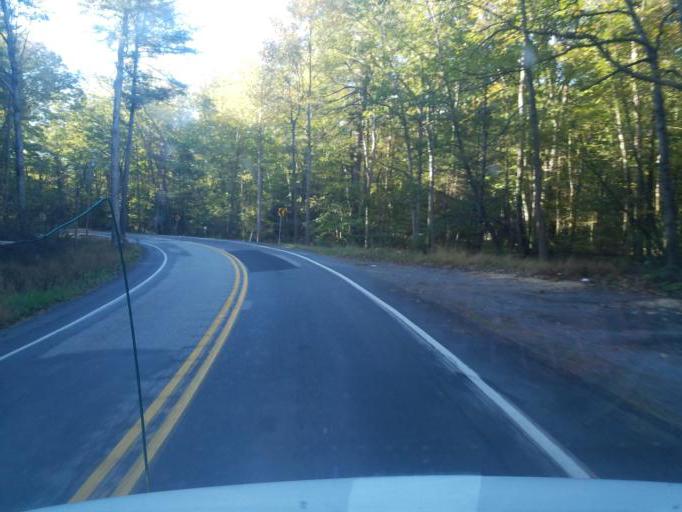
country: US
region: Pennsylvania
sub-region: Franklin County
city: Fayetteville
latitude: 39.8876
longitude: -77.4879
